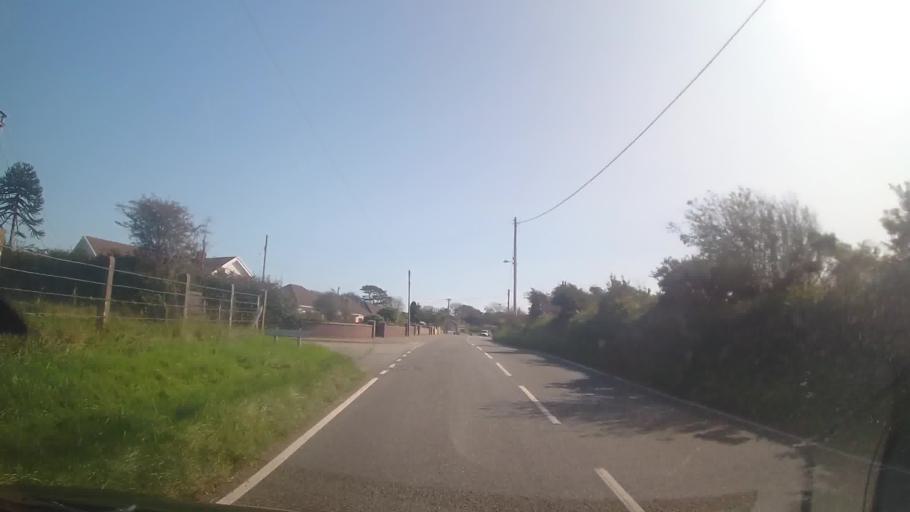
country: GB
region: Wales
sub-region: Pembrokeshire
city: Scleddau
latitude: 51.9311
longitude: -5.0080
